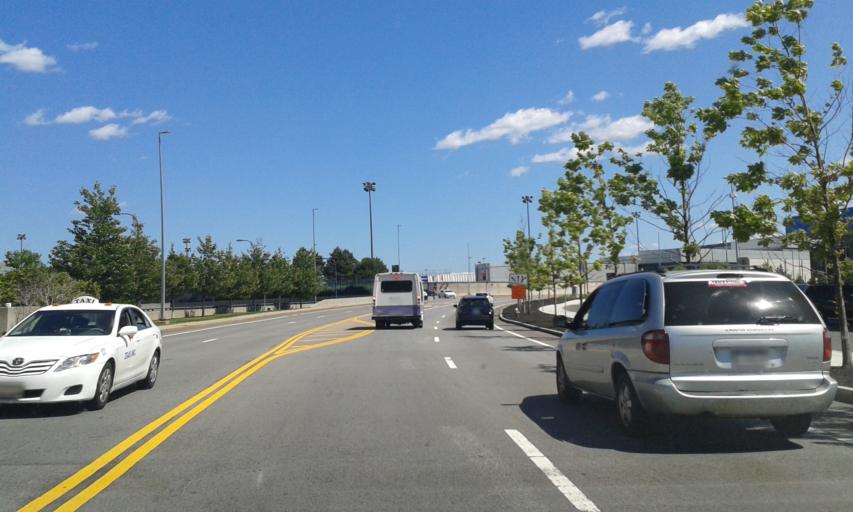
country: US
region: Massachusetts
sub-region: Suffolk County
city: Chelsea
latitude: 42.3663
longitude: -71.0261
